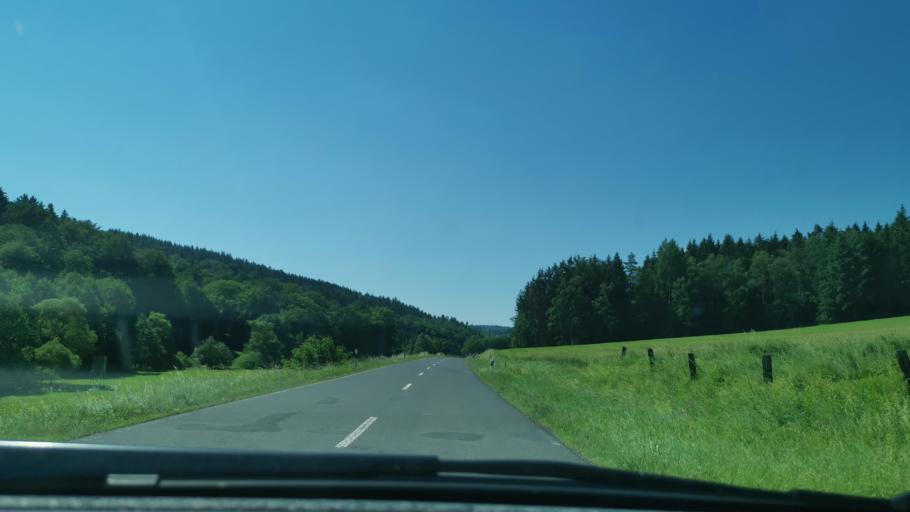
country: DE
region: Hesse
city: Spangenberg
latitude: 51.1247
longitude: 9.7087
